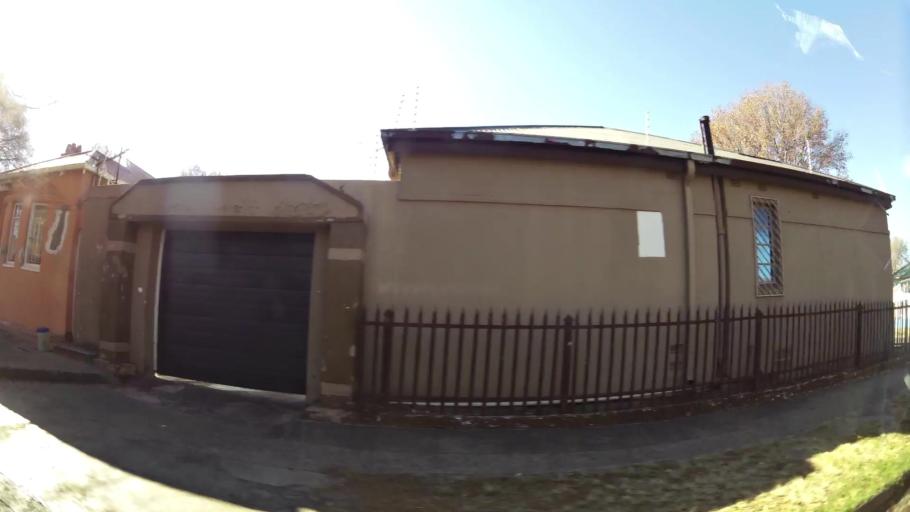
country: ZA
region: Gauteng
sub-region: City of Johannesburg Metropolitan Municipality
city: Johannesburg
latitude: -26.1982
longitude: 28.0066
